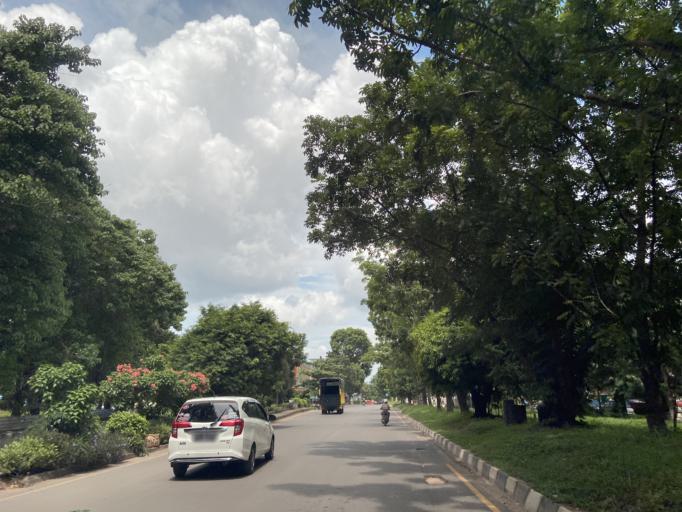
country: SG
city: Singapore
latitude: 1.1492
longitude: 104.0033
